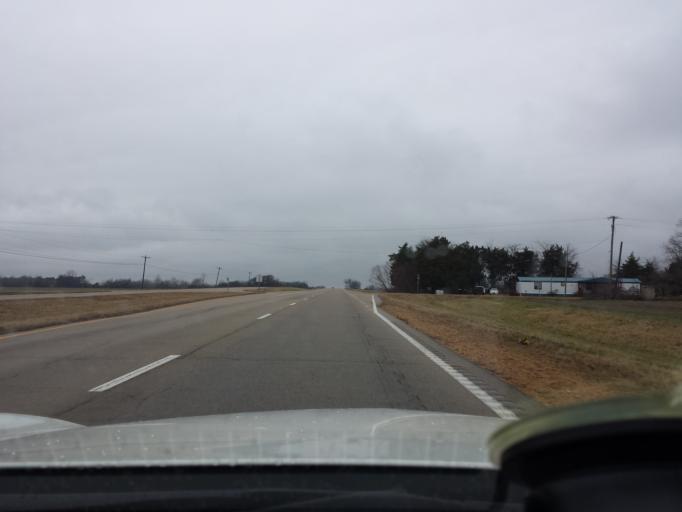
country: US
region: Mississippi
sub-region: Chickasaw County
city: Okolona
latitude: 33.8901
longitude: -88.7268
